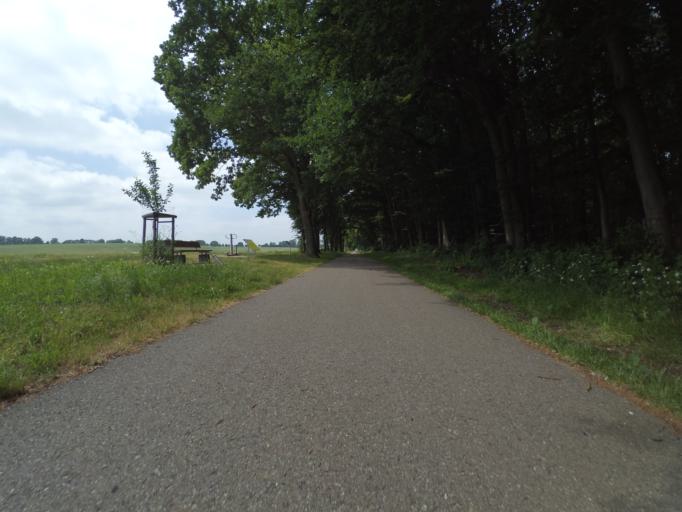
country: DE
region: Mecklenburg-Vorpommern
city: Malchow
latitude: 53.4901
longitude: 12.5017
